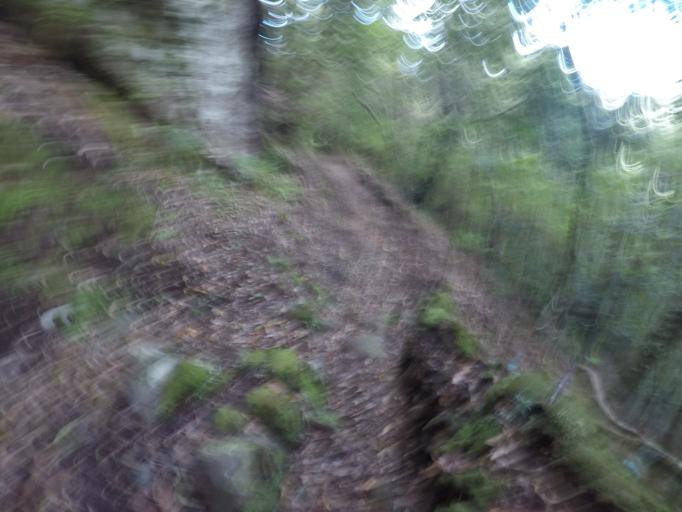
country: PT
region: Madeira
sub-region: Camara de Lobos
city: Curral das Freiras
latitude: 32.7736
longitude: -16.9794
